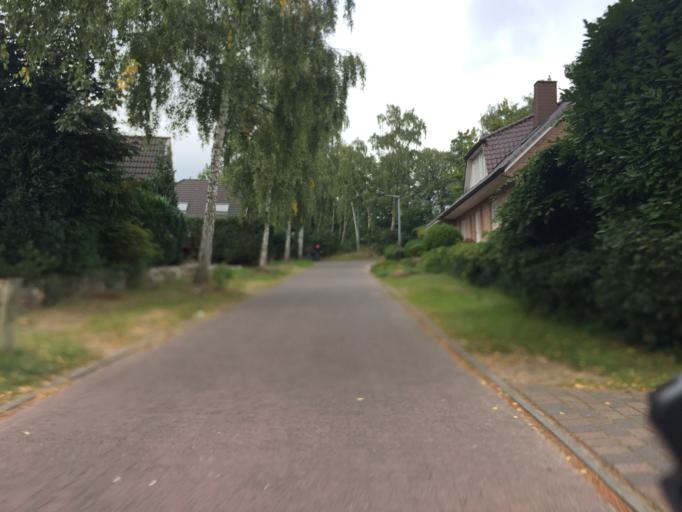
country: DE
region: Schleswig-Holstein
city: Munsterdorf
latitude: 53.9233
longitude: 9.5442
